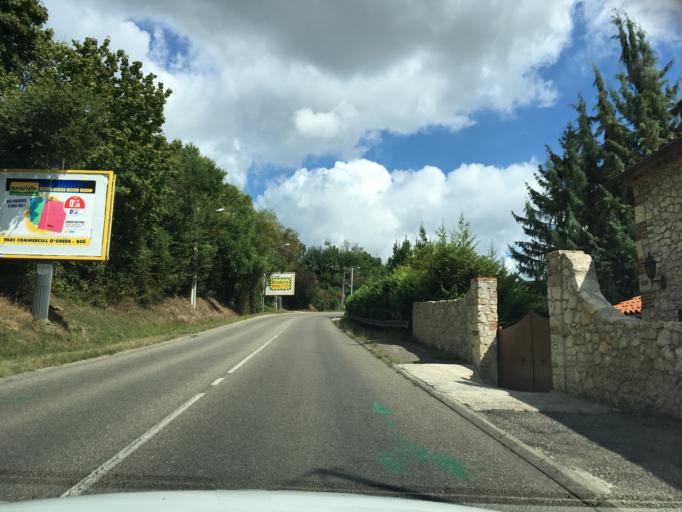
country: FR
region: Aquitaine
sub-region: Departement du Lot-et-Garonne
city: Agen
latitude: 44.2212
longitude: 0.6311
